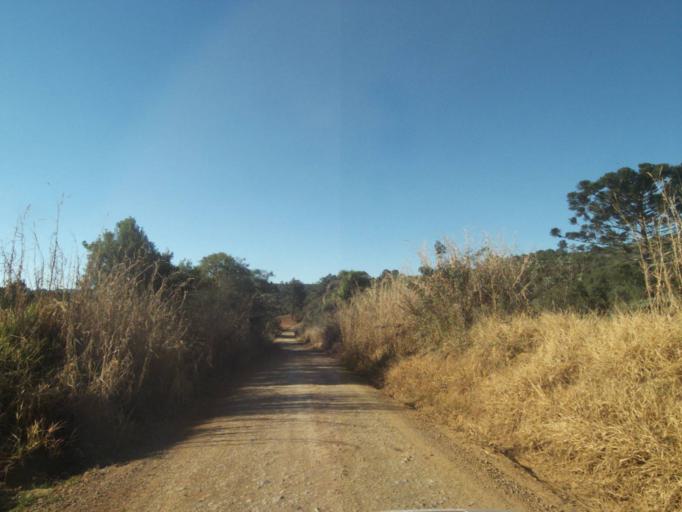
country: BR
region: Parana
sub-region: Tibagi
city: Tibagi
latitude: -24.5322
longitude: -50.4937
